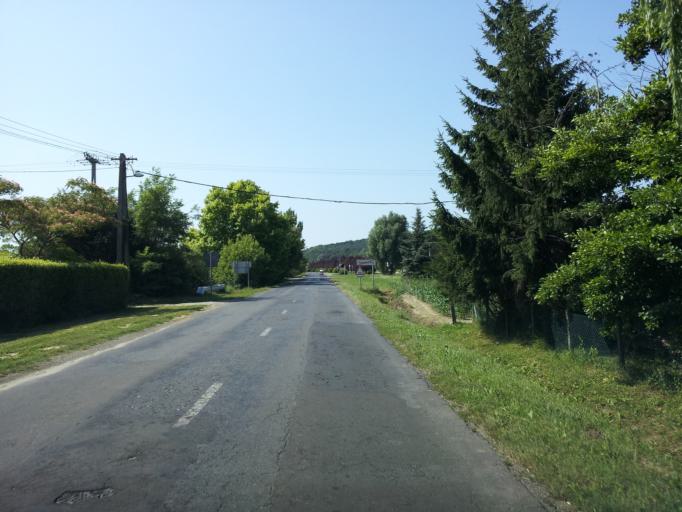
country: HU
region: Zala
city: Heviz
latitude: 46.8382
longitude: 17.0935
